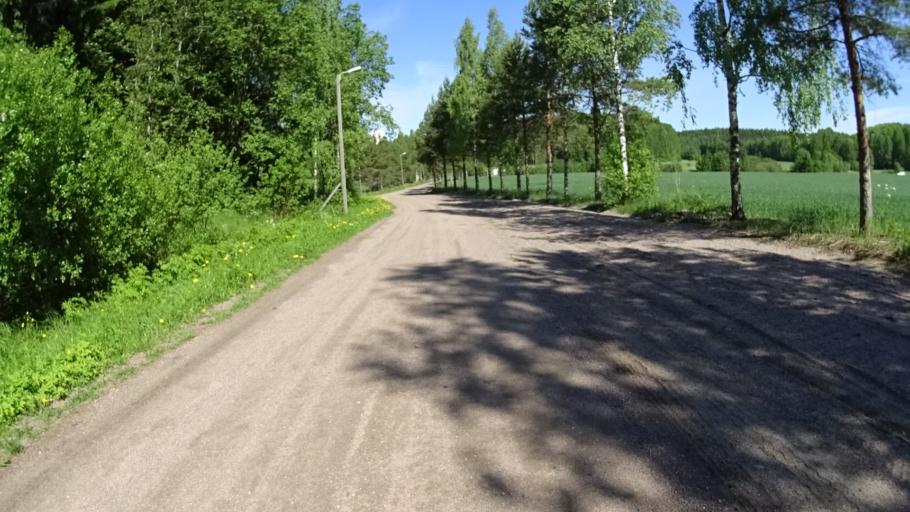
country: FI
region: Uusimaa
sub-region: Helsinki
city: Kilo
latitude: 60.2897
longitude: 24.8136
